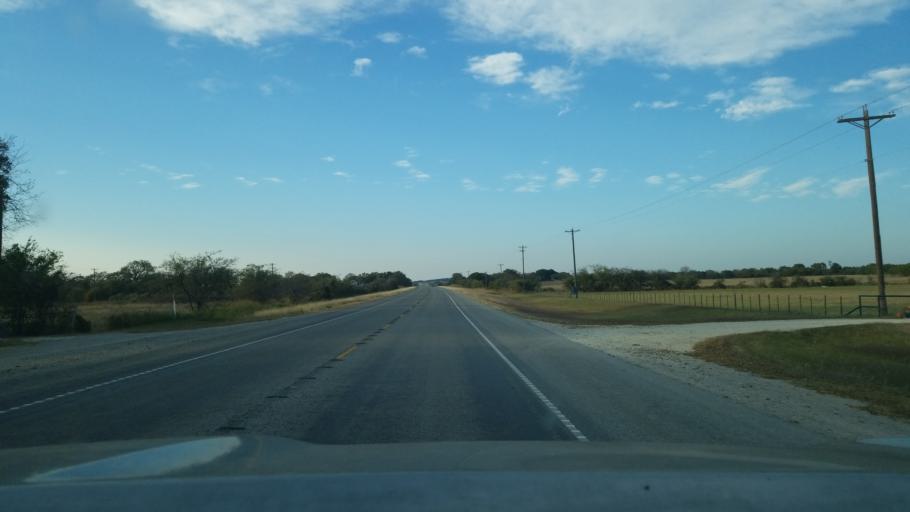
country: US
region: Texas
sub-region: Brown County
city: Lake Brownwood
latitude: 32.0389
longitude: -98.9369
